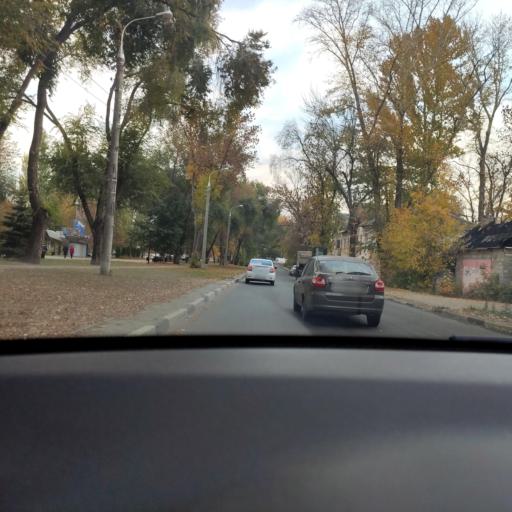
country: RU
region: Samara
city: Samara
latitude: 53.2327
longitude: 50.2636
